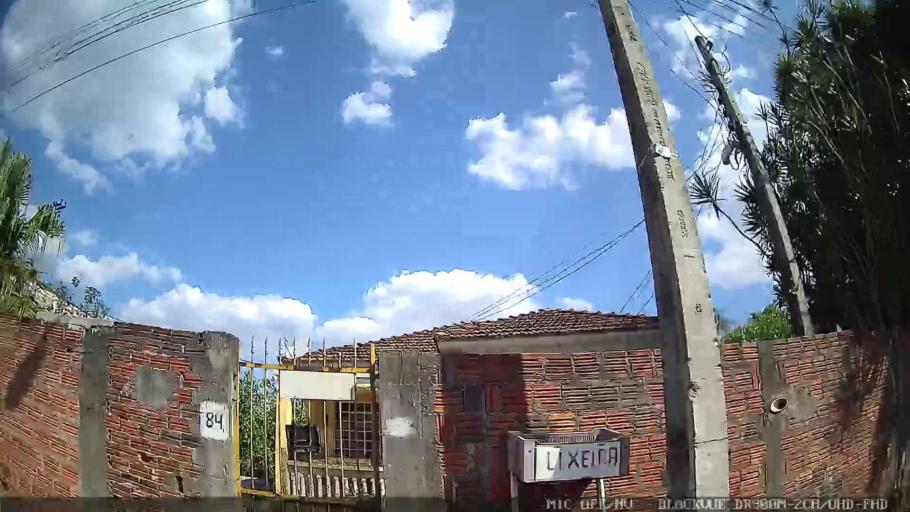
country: BR
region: Sao Paulo
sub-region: Itupeva
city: Itupeva
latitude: -23.2434
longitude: -47.0611
